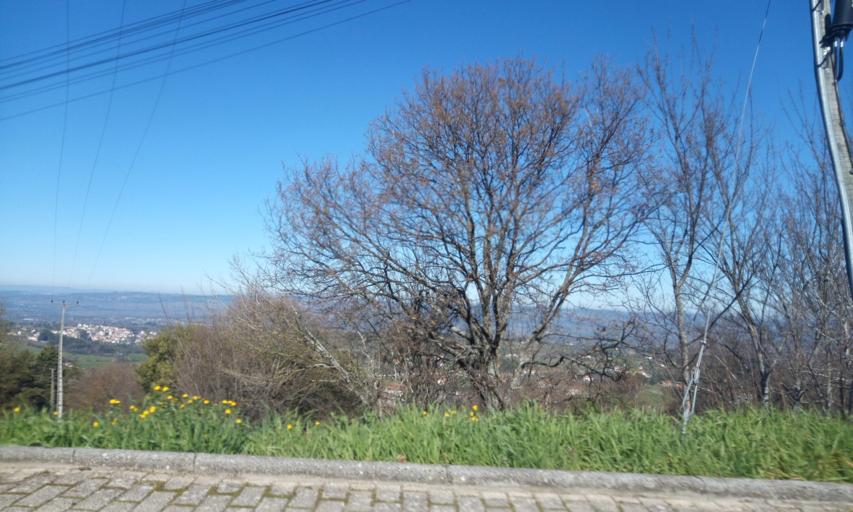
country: PT
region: Guarda
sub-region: Manteigas
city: Manteigas
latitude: 40.4997
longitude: -7.5864
